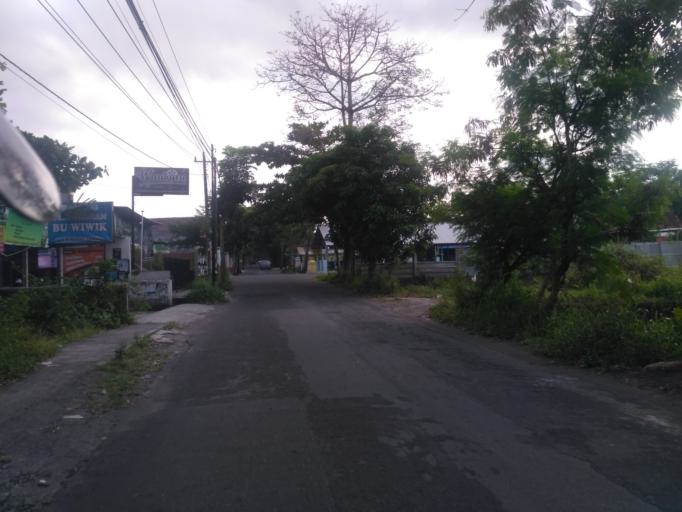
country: ID
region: Daerah Istimewa Yogyakarta
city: Yogyakarta
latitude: -7.7743
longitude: 110.3422
